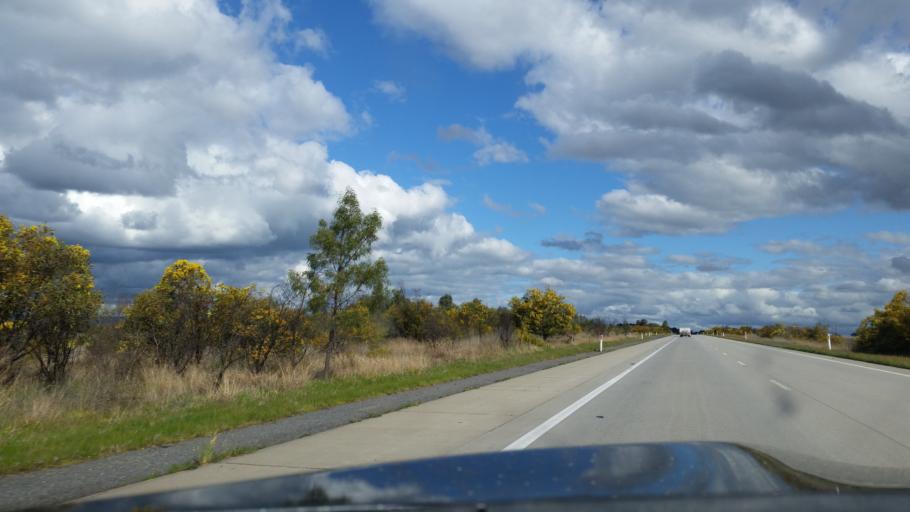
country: AU
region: New South Wales
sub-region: Greater Hume Shire
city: Jindera
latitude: -35.9529
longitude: 147.0043
